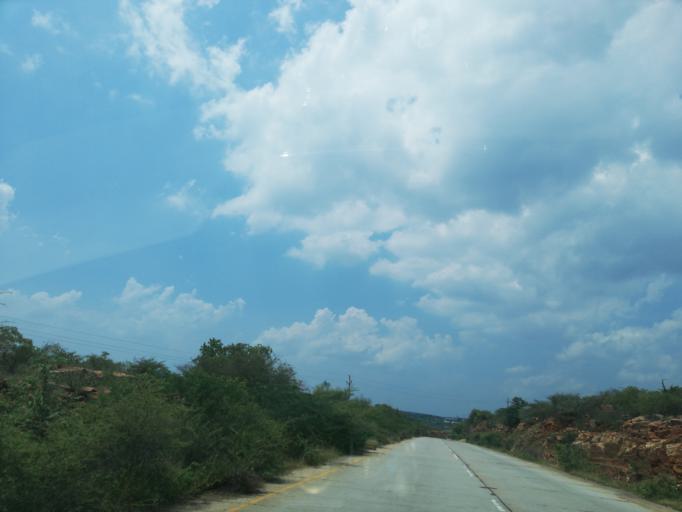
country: IN
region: Andhra Pradesh
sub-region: Guntur
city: Macherla
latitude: 16.5699
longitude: 79.3325
